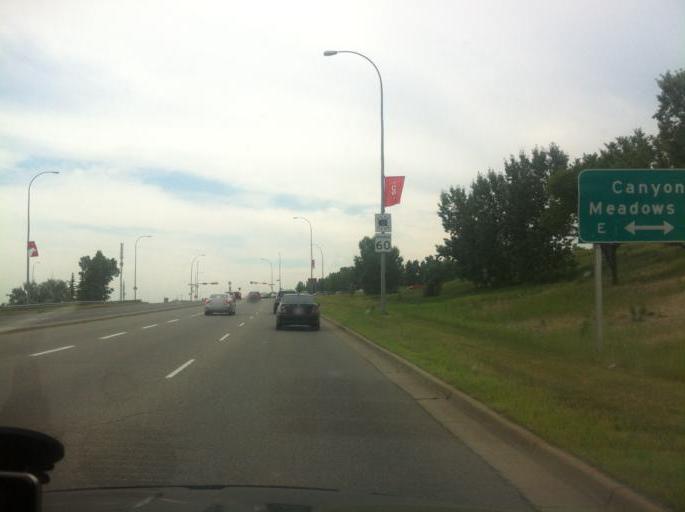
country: CA
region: Alberta
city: Calgary
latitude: 50.9332
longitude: -114.0330
